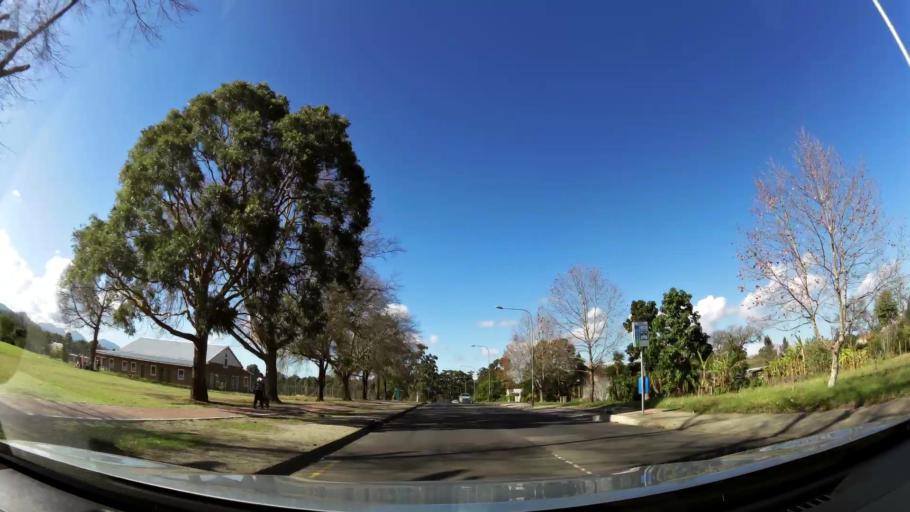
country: ZA
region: Western Cape
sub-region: Eden District Municipality
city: George
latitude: -33.9477
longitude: 22.4200
